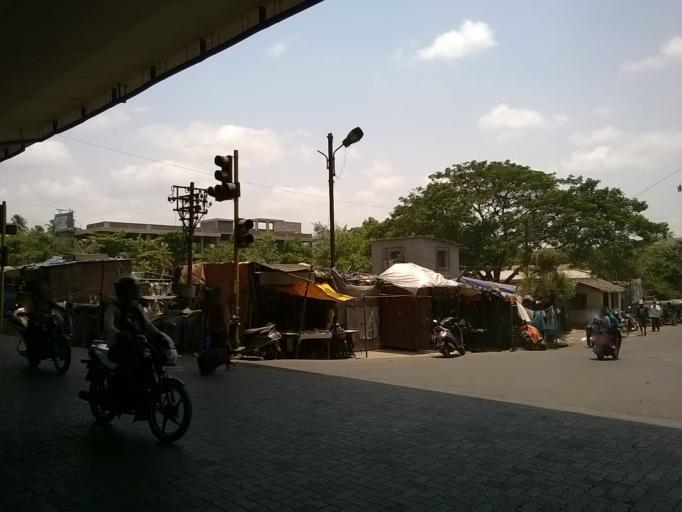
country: IN
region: Maharashtra
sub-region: Raigarh
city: Panvel
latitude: 18.9896
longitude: 73.1156
